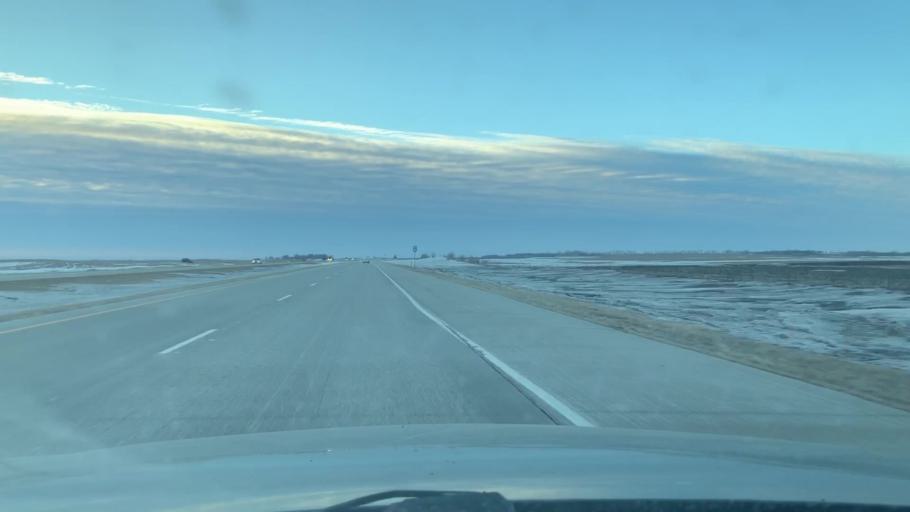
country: US
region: North Dakota
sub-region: Ransom County
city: Sheldon
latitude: 46.8758
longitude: -97.5014
